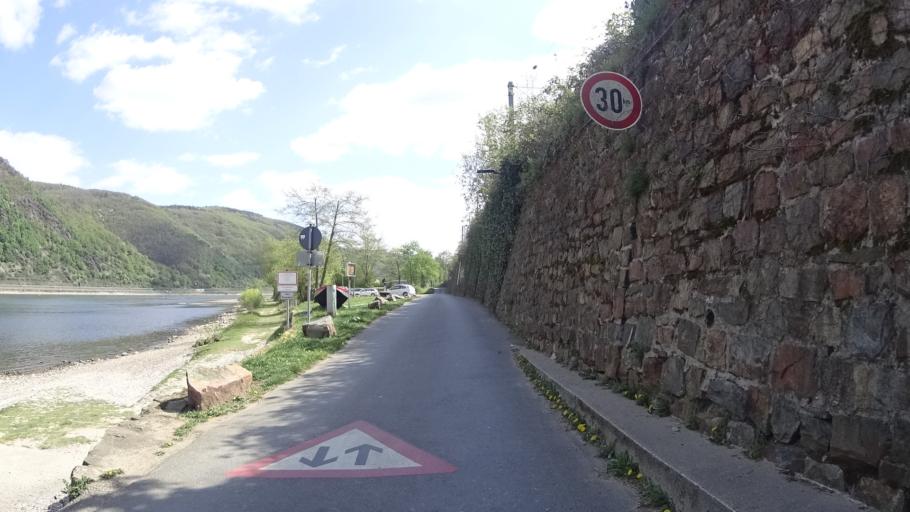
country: DE
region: Rheinland-Pfalz
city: Trechtingshausen
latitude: 50.0108
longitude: 7.8512
